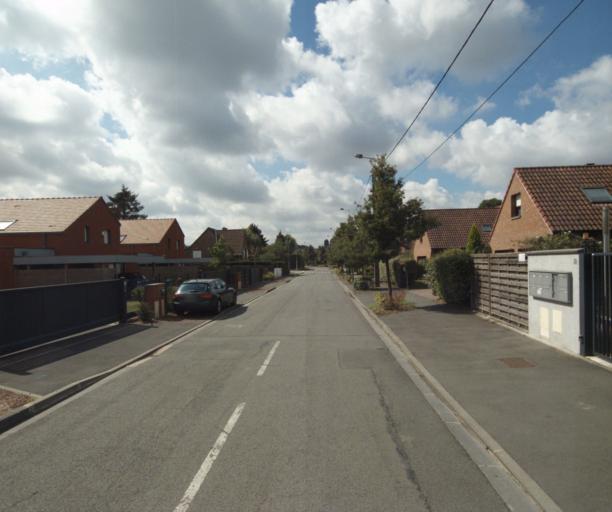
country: FR
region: Nord-Pas-de-Calais
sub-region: Departement du Nord
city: Wasquehal
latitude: 50.6554
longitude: 3.1502
